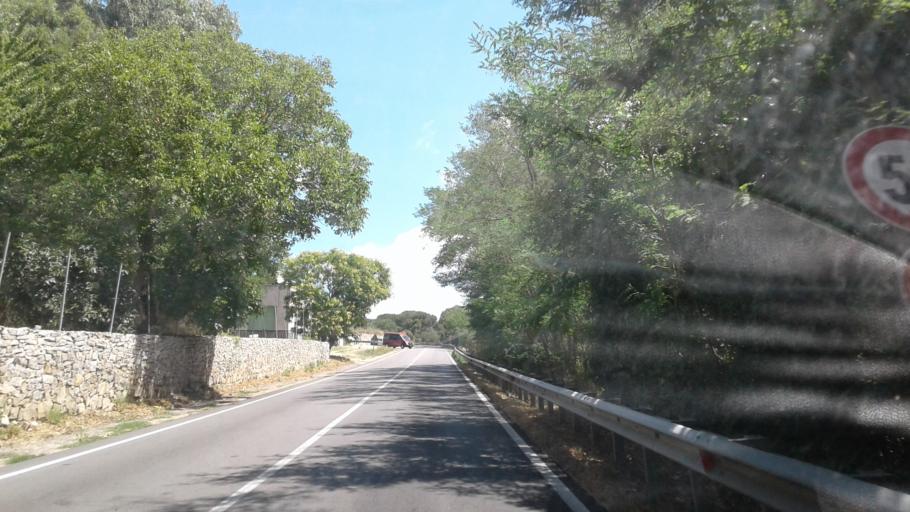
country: IT
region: Sardinia
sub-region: Provincia di Olbia-Tempio
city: Luras
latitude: 40.9144
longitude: 9.1664
